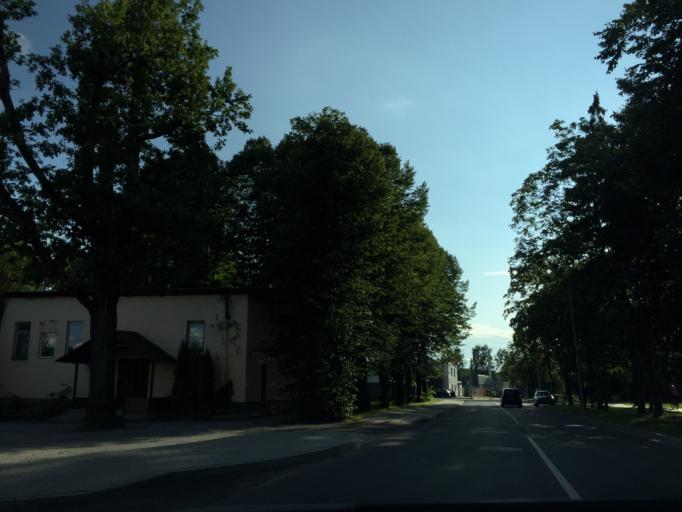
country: LV
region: Ogre
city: Ogre
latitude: 56.8147
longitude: 24.6486
